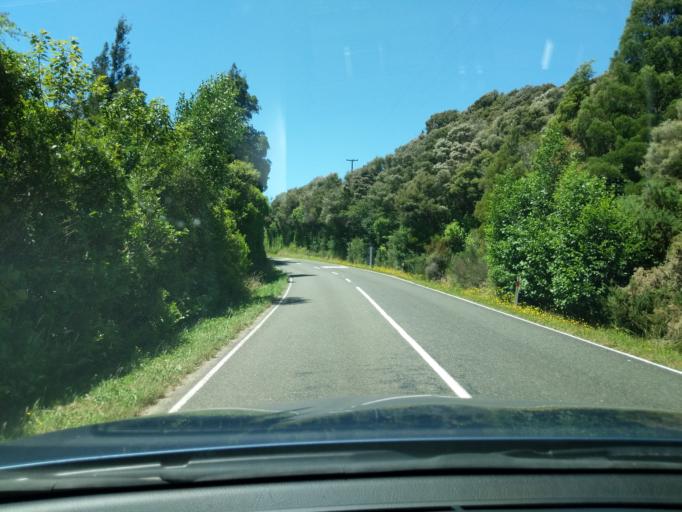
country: NZ
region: Tasman
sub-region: Tasman District
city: Takaka
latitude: -40.7274
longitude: 172.5854
